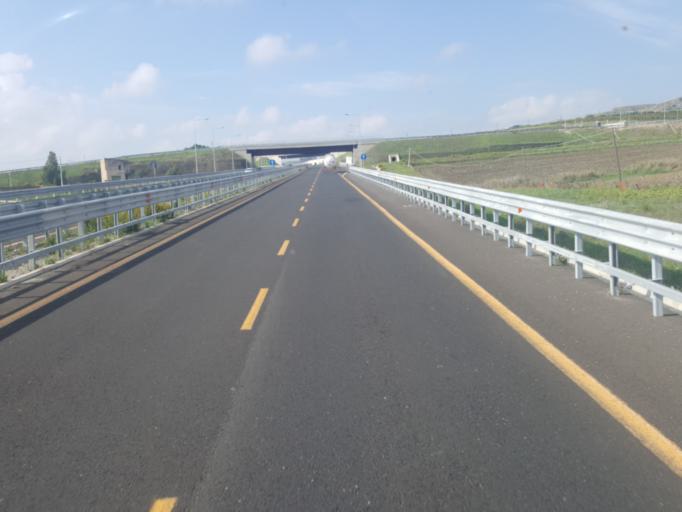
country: IT
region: Sicily
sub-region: Provincia di Caltanissetta
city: Serradifalco
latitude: 37.4228
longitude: 13.9164
